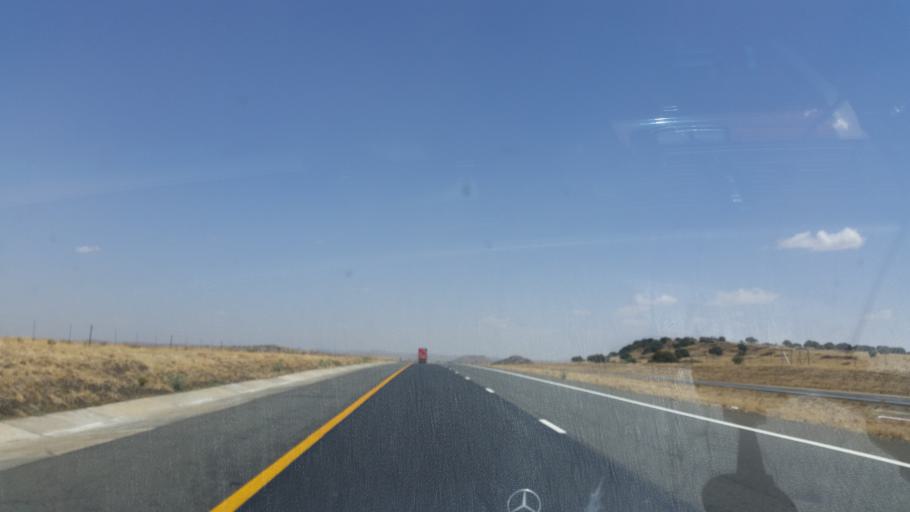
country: ZA
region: Orange Free State
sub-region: Lejweleputswa District Municipality
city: Brandfort
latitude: -28.9169
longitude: 26.4470
